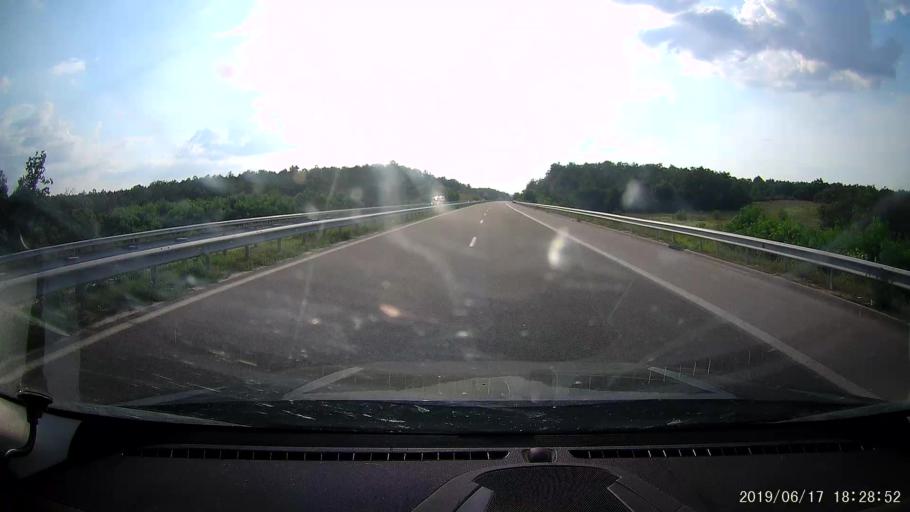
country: BG
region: Khaskovo
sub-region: Obshtina Dimitrovgrad
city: Dimitrovgrad
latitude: 42.0249
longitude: 25.5689
